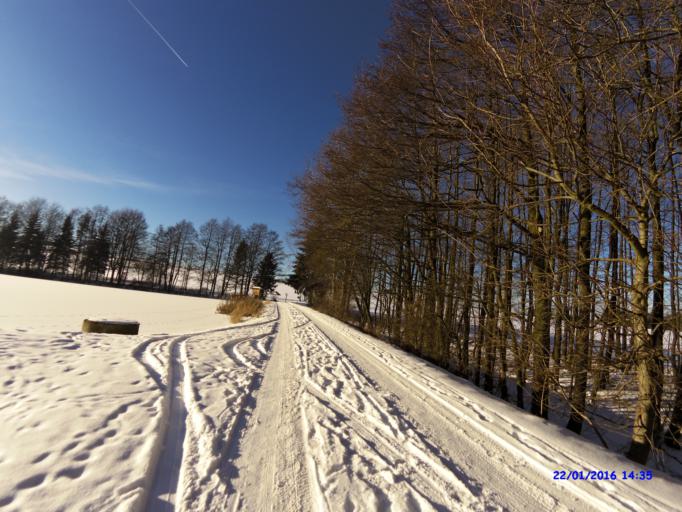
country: DE
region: Thuringia
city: Tanna
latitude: 50.4881
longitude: 11.8668
